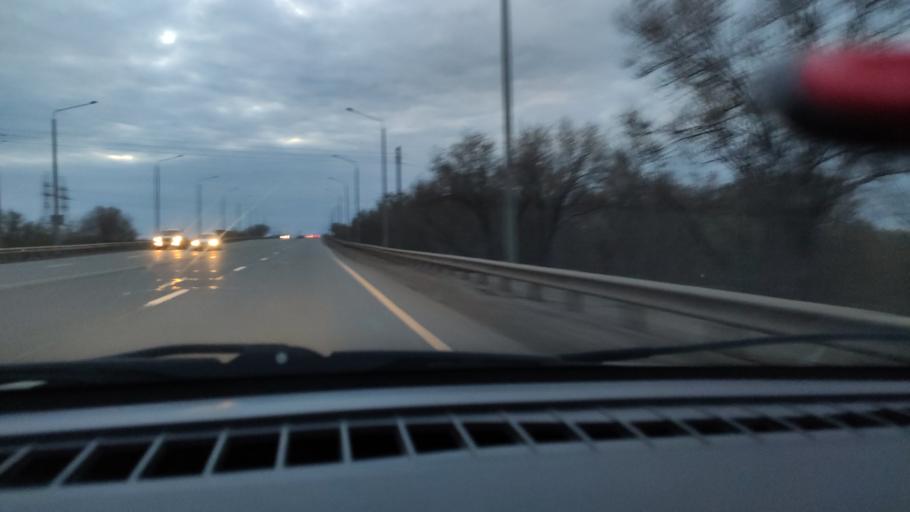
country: RU
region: Orenburg
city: Orenburg
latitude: 51.8507
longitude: 55.1428
